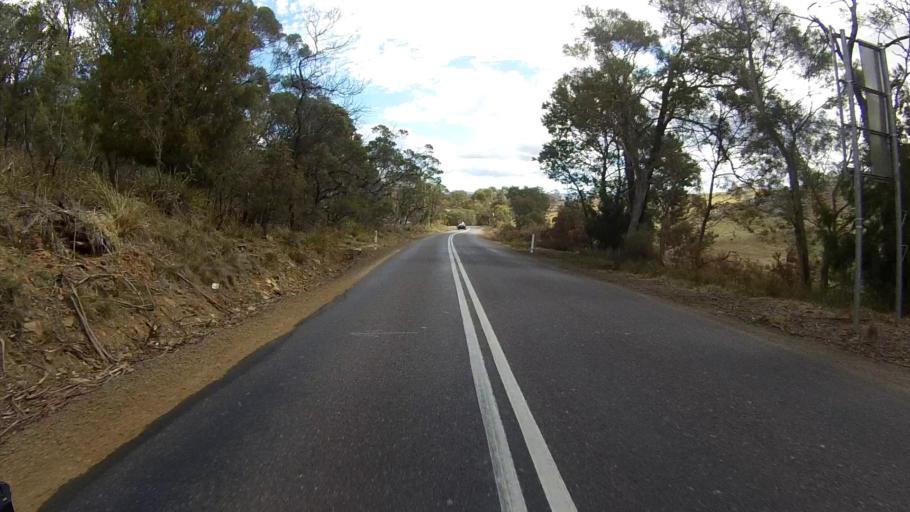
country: AU
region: Tasmania
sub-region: Break O'Day
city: St Helens
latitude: -41.9913
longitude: 148.1187
